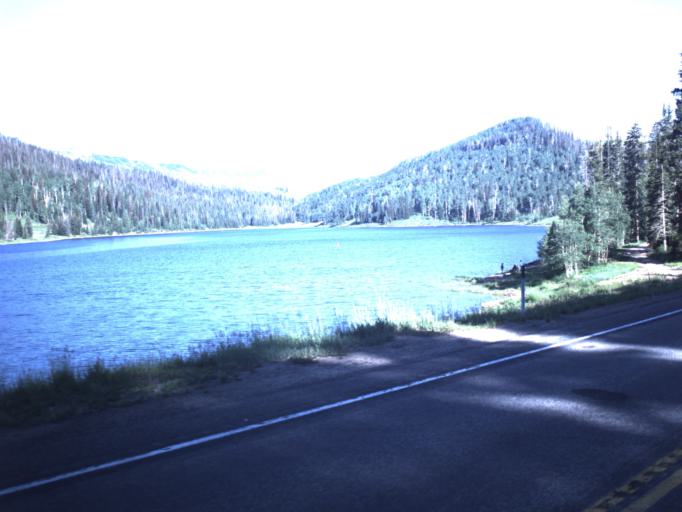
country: US
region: Utah
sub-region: Sanpete County
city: Fairview
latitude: 39.5910
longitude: -111.2641
